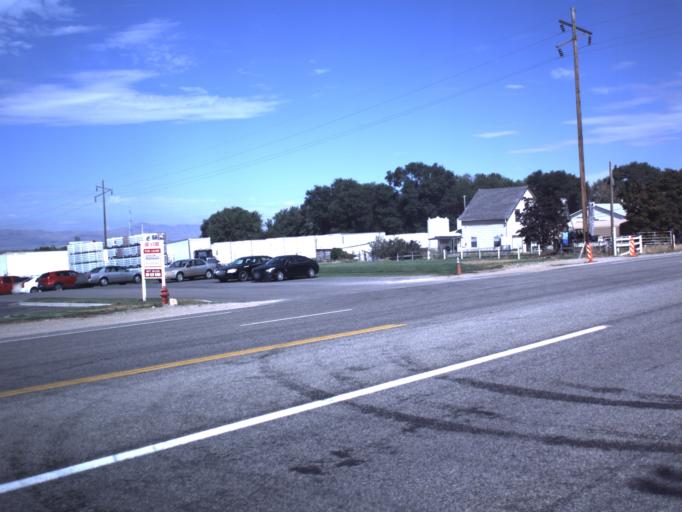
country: US
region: Utah
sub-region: Box Elder County
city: South Willard
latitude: 41.3494
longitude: -112.0345
